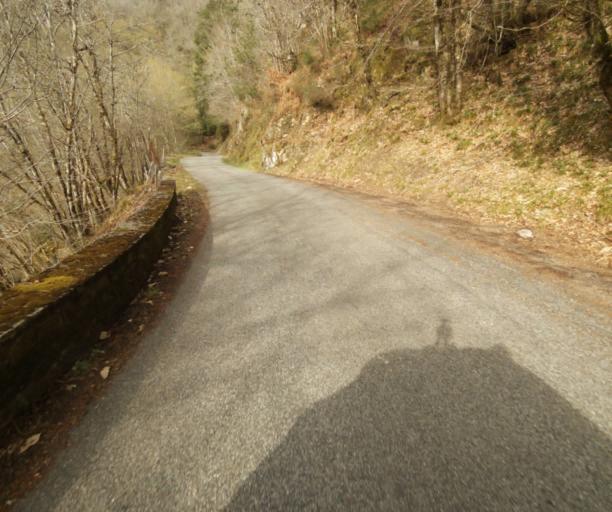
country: FR
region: Limousin
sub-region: Departement de la Correze
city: Argentat
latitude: 45.1952
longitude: 1.9793
